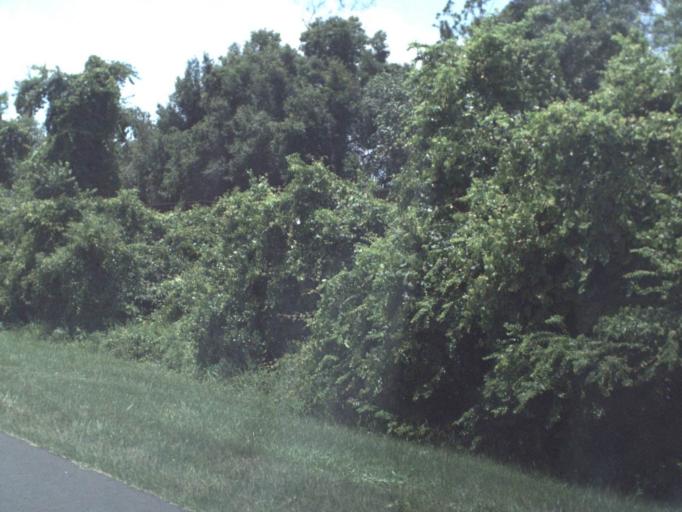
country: US
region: Florida
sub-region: Alachua County
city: Newberry
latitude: 29.6351
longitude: -82.6062
